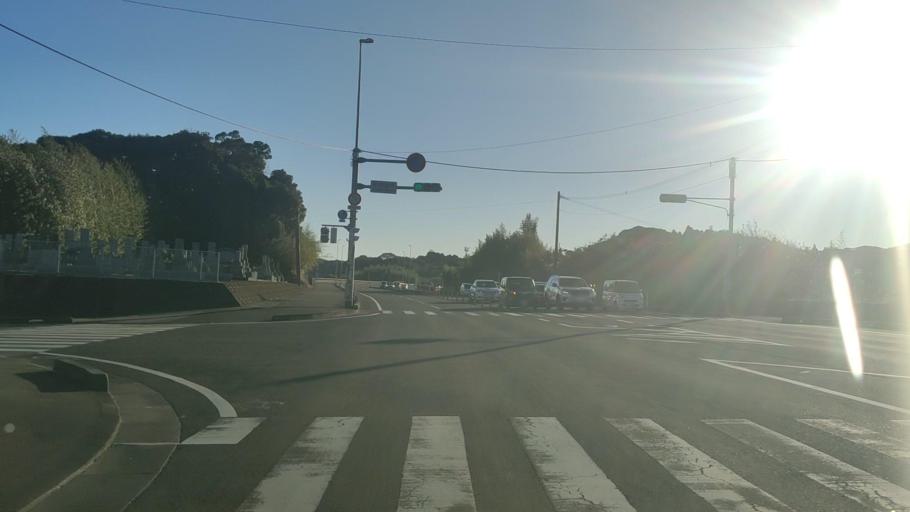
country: JP
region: Miyazaki
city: Miyazaki-shi
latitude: 31.8894
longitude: 131.4031
